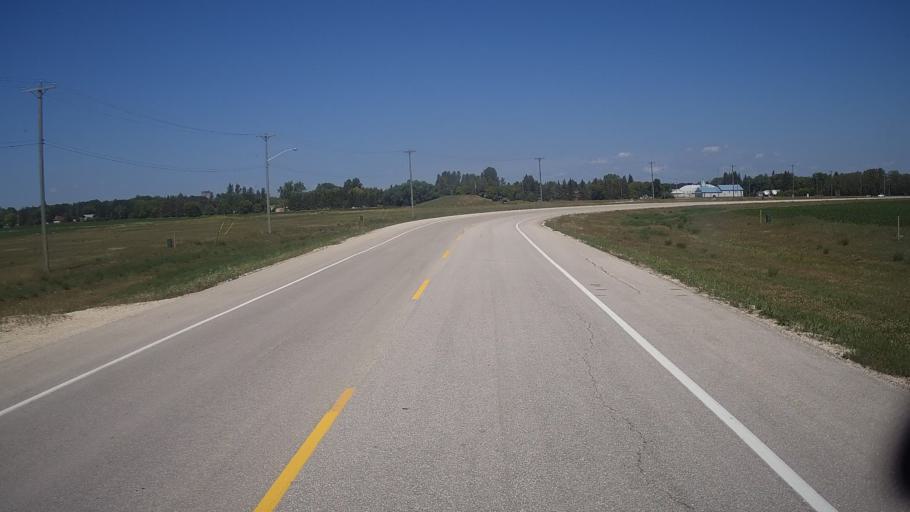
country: CA
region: Manitoba
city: Stonewall
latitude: 50.1252
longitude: -97.5440
